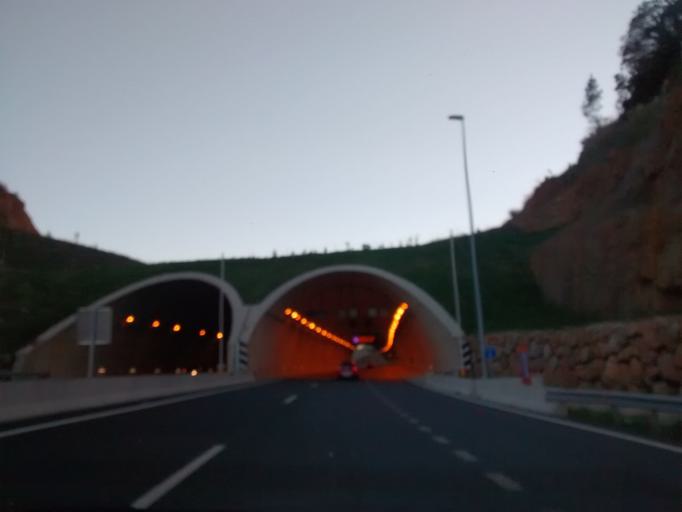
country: ES
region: Cantabria
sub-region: Provincia de Cantabria
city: Camargo
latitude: 43.4144
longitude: -3.8721
